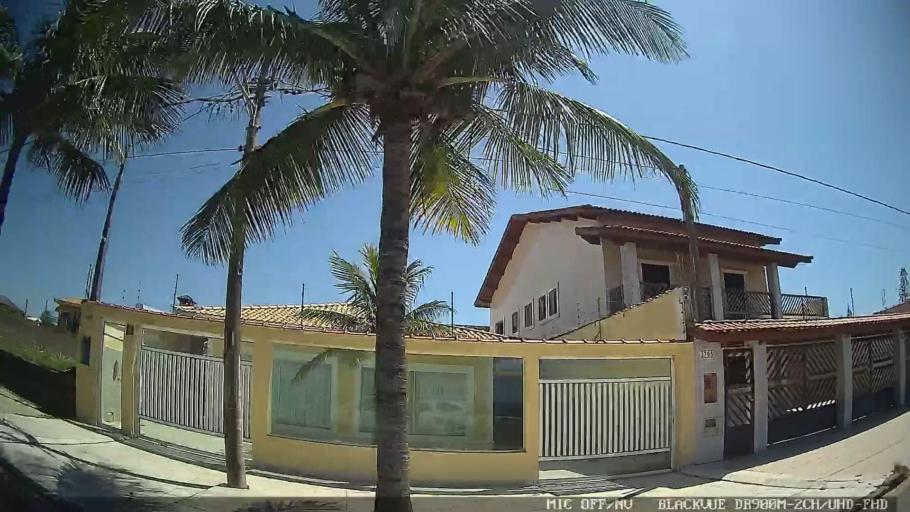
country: BR
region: Sao Paulo
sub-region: Peruibe
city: Peruibe
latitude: -24.3116
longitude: -46.9782
